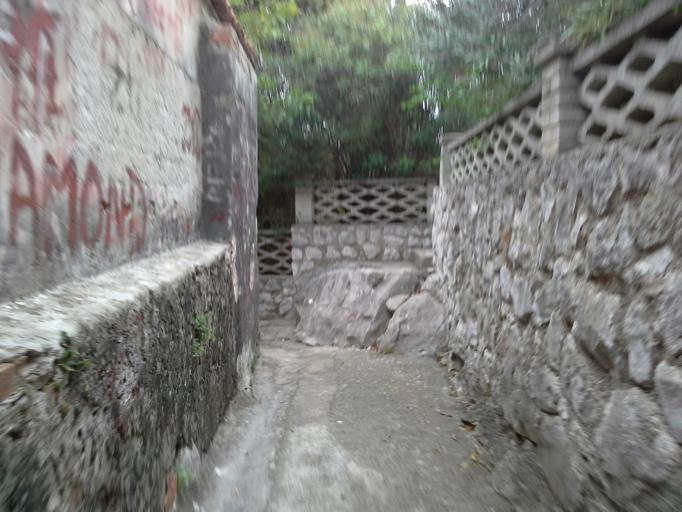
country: HR
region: Primorsko-Goranska
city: Mali Losinj
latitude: 44.5396
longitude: 14.4655
